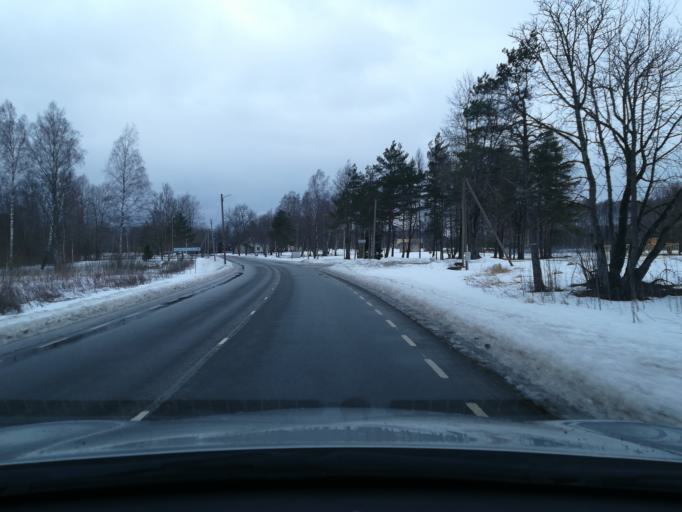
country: EE
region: Harju
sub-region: Nissi vald
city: Turba
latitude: 59.0728
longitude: 24.2477
